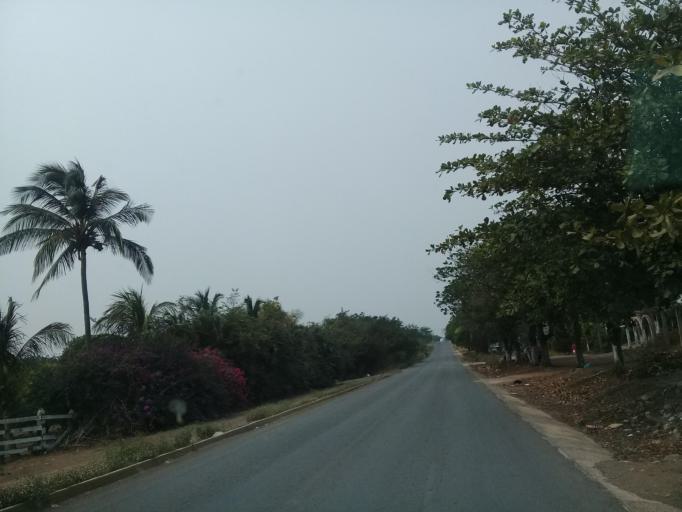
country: MX
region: Veracruz
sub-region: Medellin
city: La Laguna y Monte del Castillo
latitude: 18.9770
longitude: -96.1190
